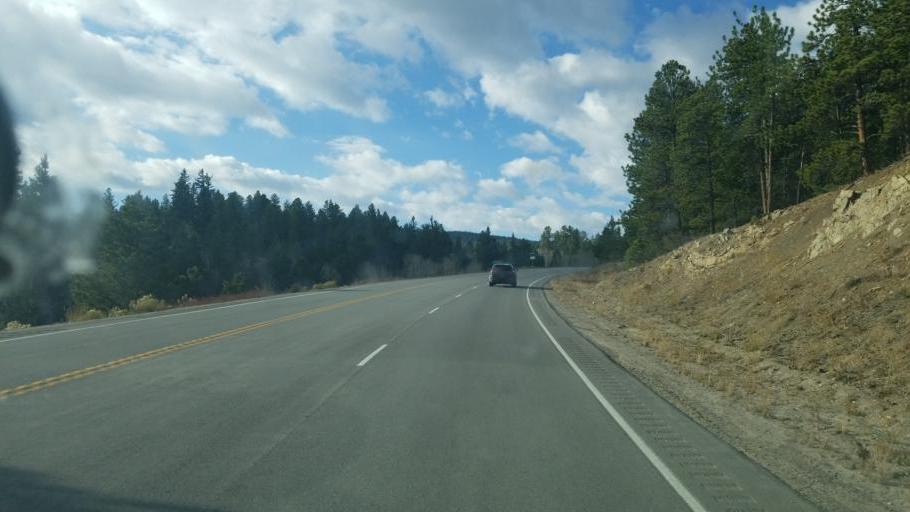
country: US
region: Colorado
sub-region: Chaffee County
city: Buena Vista
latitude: 38.9142
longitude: -105.9699
